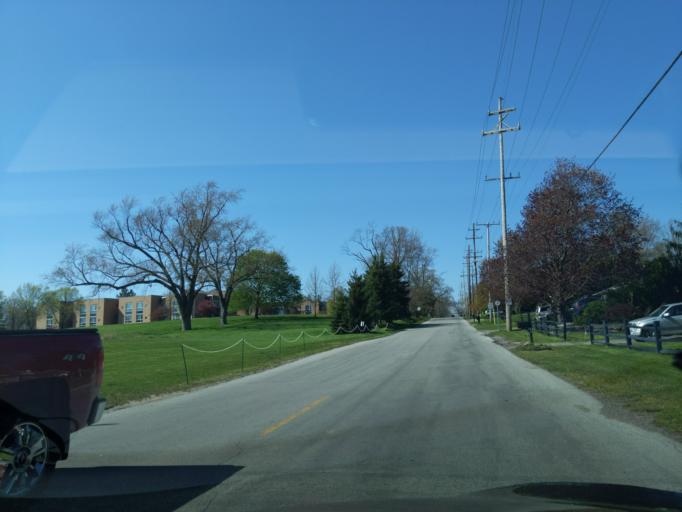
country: US
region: Michigan
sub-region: Kent County
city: East Grand Rapids
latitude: 42.9628
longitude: -85.6176
